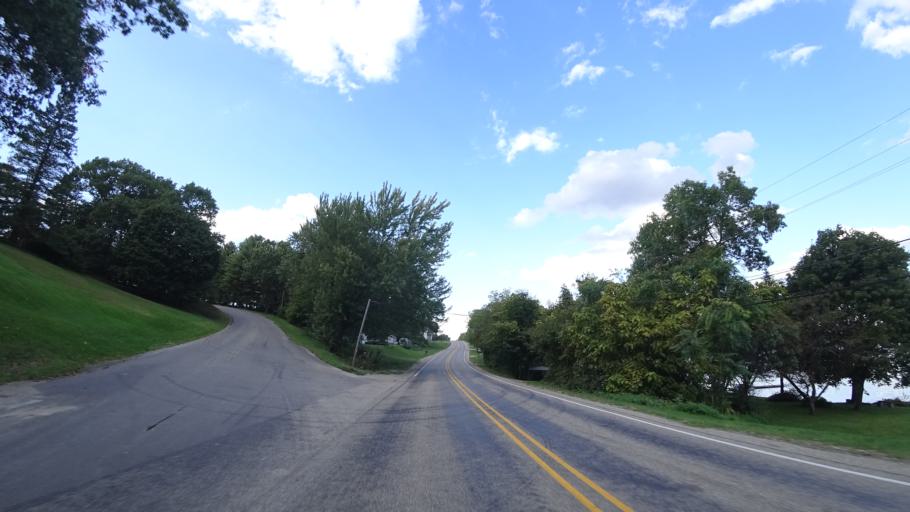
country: US
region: Michigan
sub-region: Saint Joseph County
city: Sturgis
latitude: 41.8385
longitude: -85.4288
